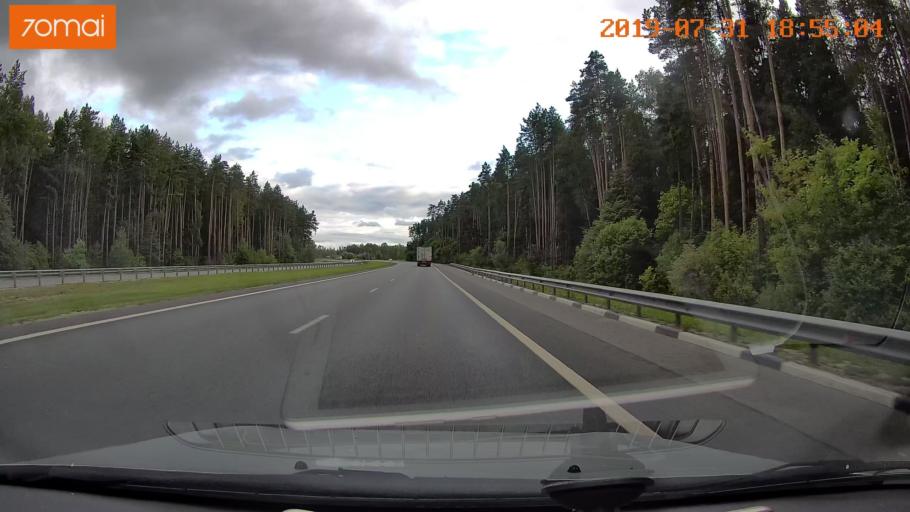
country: RU
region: Moskovskaya
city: Raduzhnyy
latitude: 55.1805
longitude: 38.6682
